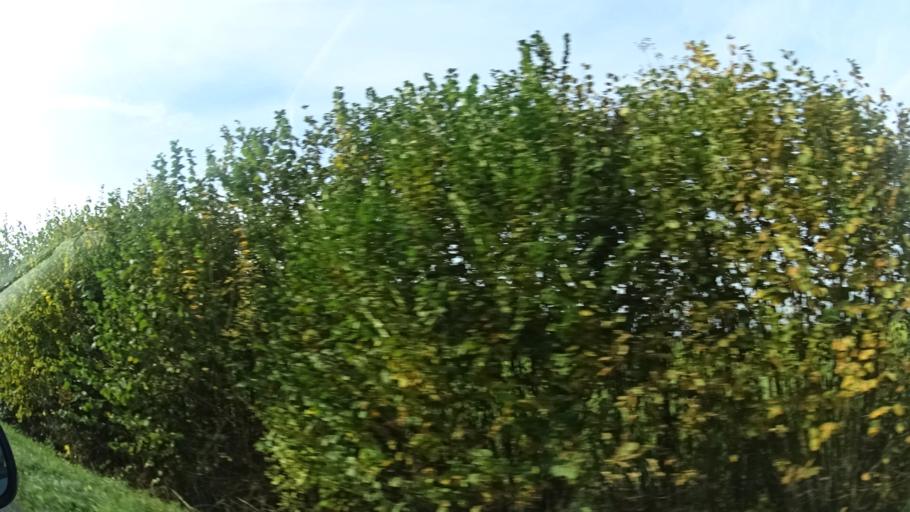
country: DE
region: Baden-Wuerttemberg
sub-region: Karlsruhe Region
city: Billigheim
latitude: 49.4099
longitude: 9.2699
